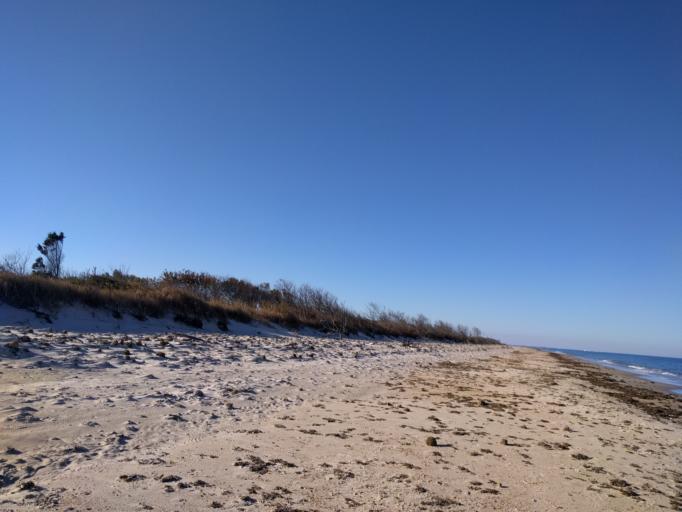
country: US
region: Virginia
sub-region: City of Poquoson
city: Poquoson
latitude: 37.0945
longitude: -76.2748
